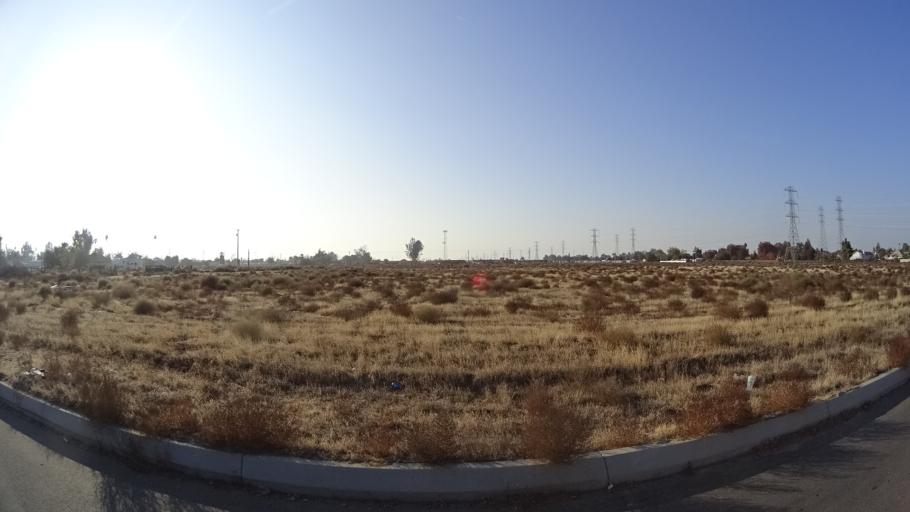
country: US
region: California
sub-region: Kern County
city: Rosedale
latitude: 35.3851
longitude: -119.1498
